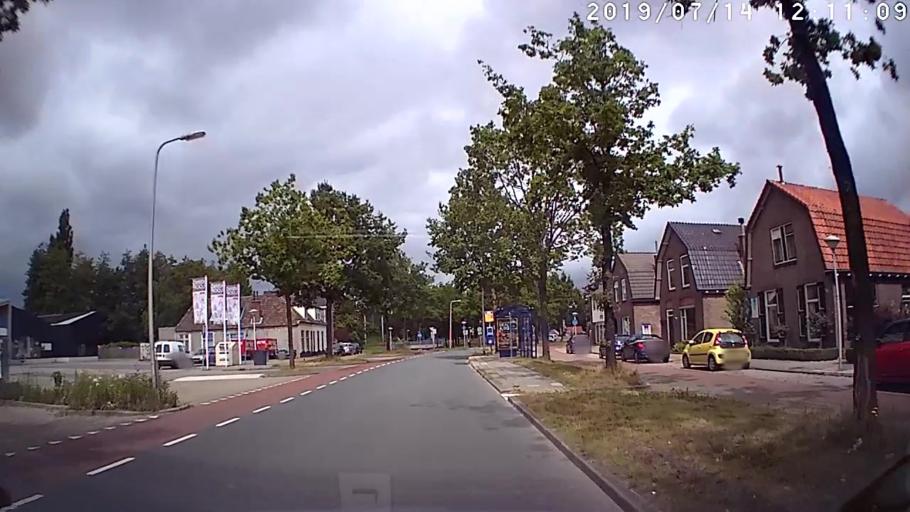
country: NL
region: Overijssel
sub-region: Gemeente Zwolle
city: Zwolle
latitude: 52.4909
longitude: 6.1079
